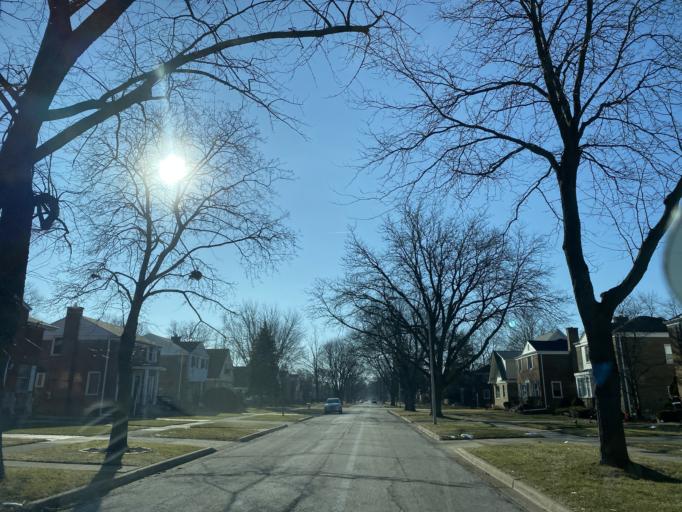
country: US
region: Illinois
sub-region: Cook County
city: Westchester
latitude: 41.8590
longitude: -87.8700
